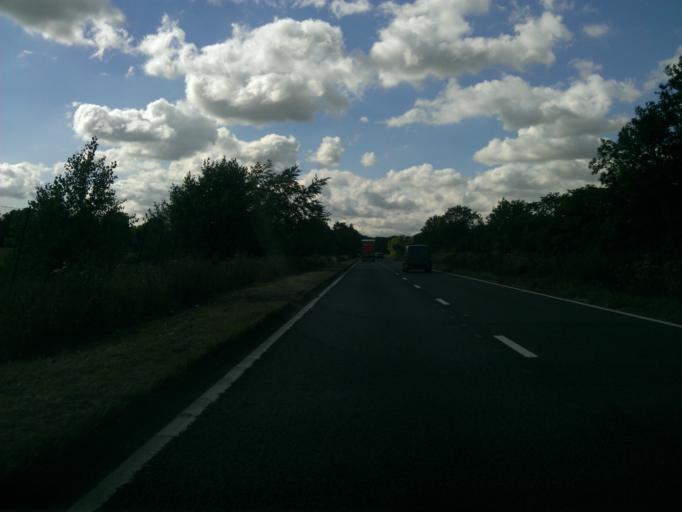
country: GB
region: England
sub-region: Warwickshire
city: Atherstone
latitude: 52.5758
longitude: -1.5333
